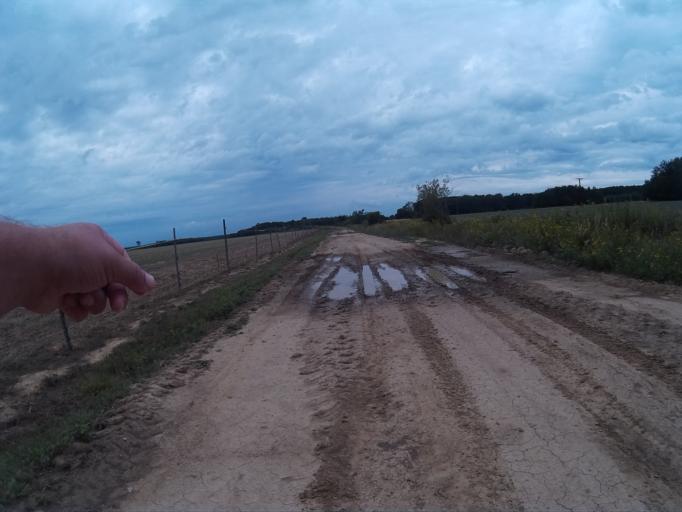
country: HU
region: Zala
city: Zalalovo
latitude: 46.7752
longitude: 16.5219
